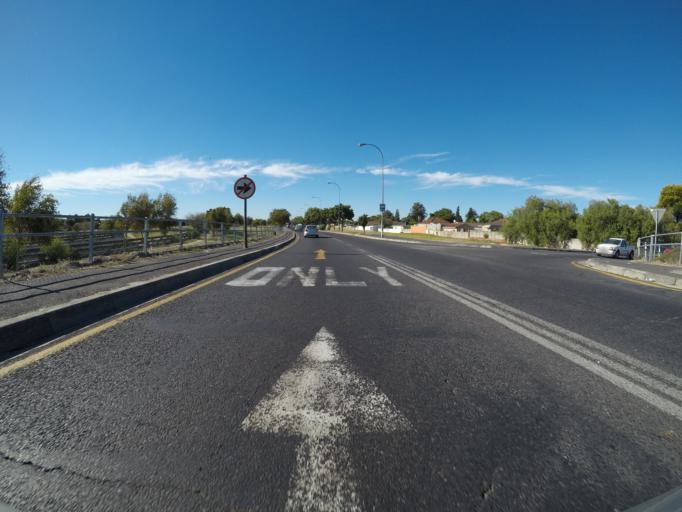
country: ZA
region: Western Cape
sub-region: City of Cape Town
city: Kraaifontein
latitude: -33.9304
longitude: 18.6767
